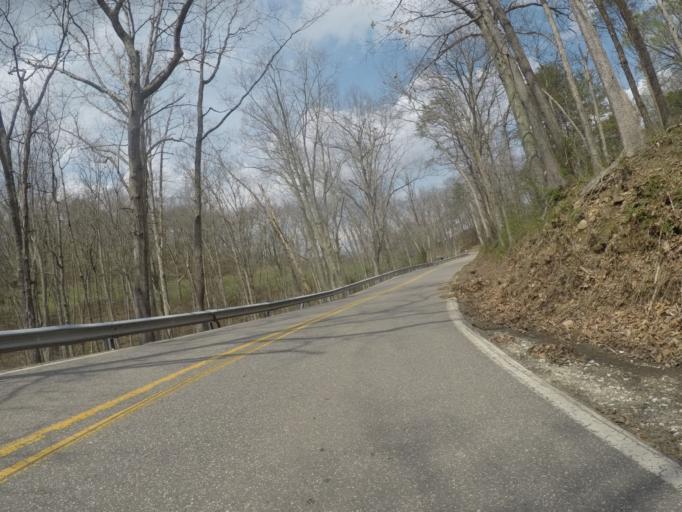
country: US
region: West Virginia
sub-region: Cabell County
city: Pea Ridge
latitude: 38.3508
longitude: -82.3362
